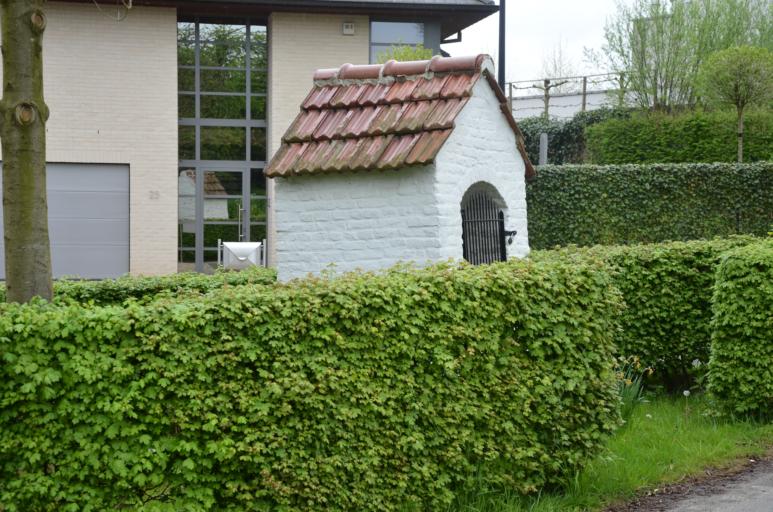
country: BE
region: Flanders
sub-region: Provincie Vlaams-Brabant
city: Sint-Pieters-Leeuw
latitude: 50.7778
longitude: 4.2001
